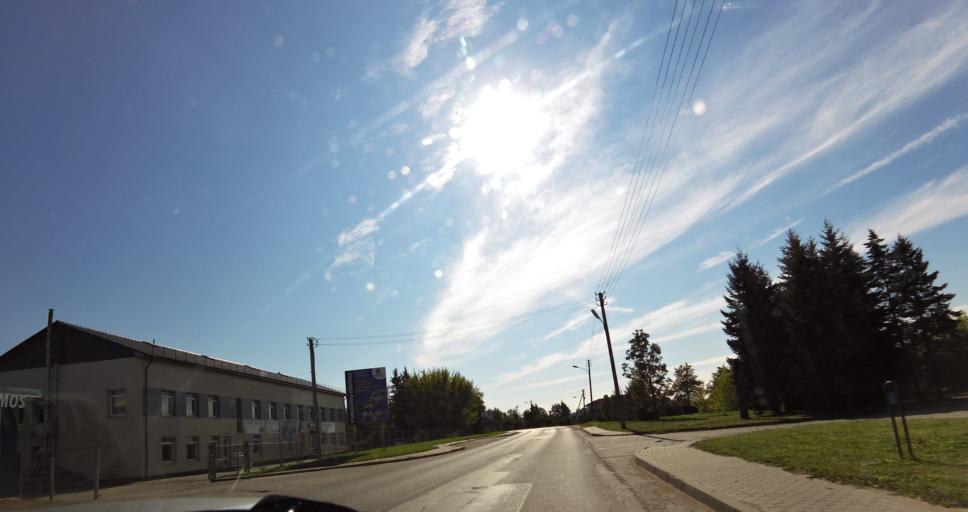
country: LT
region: Panevezys
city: Pasvalys
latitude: 56.0675
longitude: 24.3864
